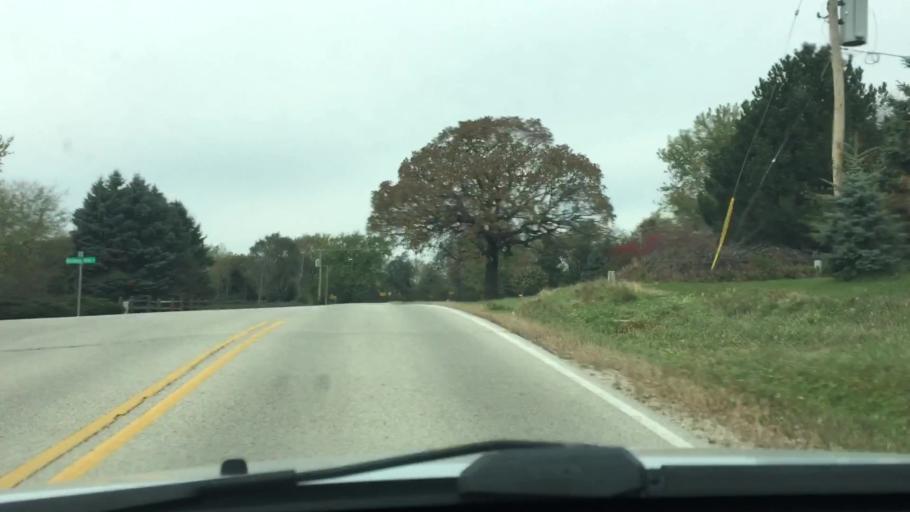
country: US
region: Wisconsin
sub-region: Waukesha County
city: North Prairie
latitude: 42.8998
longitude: -88.4031
